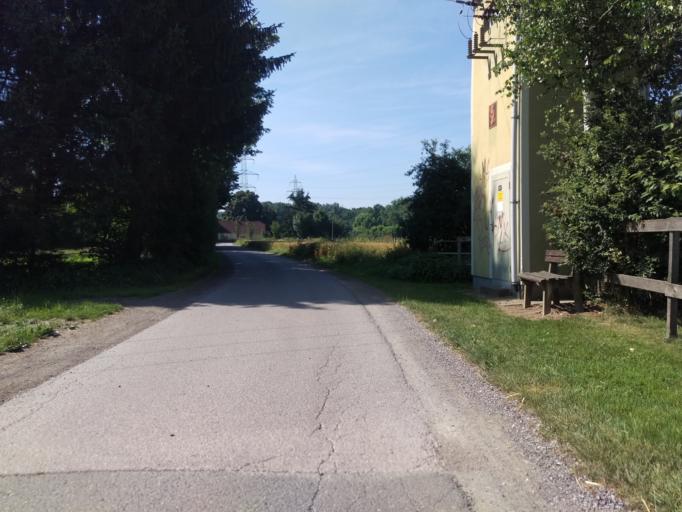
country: AT
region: Styria
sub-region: Politischer Bezirk Graz-Umgebung
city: Gossendorf
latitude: 46.9950
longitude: 15.4781
